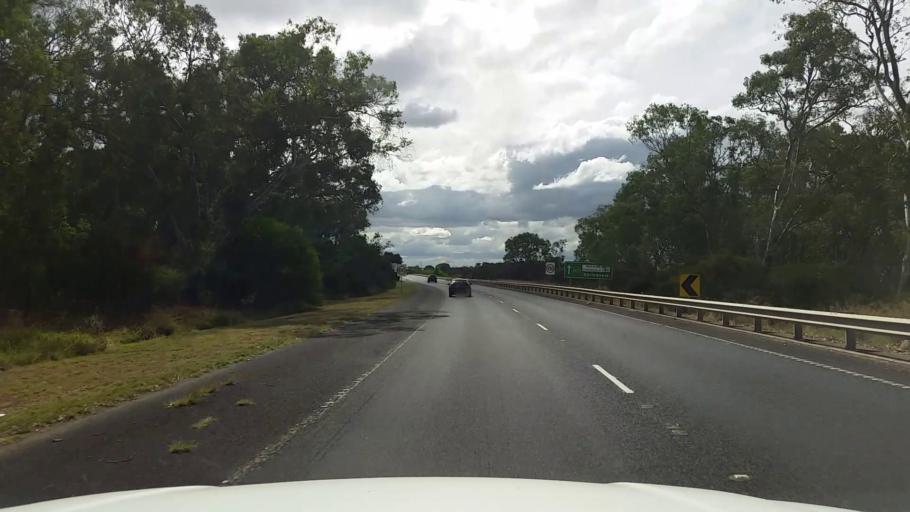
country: AU
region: Victoria
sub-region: Kingston
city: Carrum
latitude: -38.0902
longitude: 145.1492
